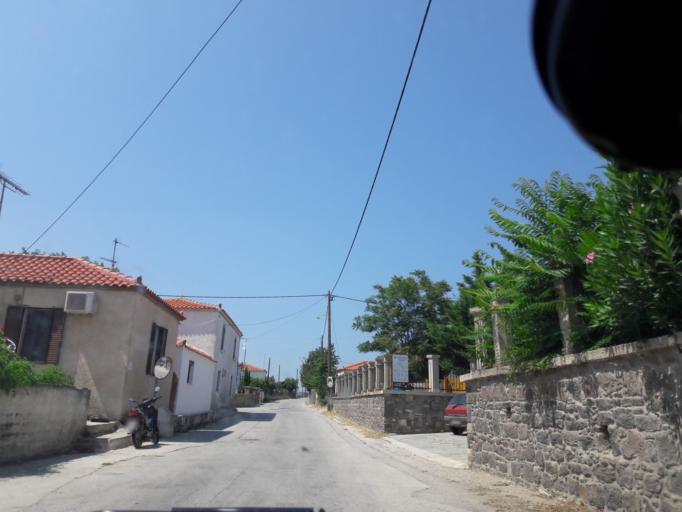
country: GR
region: North Aegean
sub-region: Nomos Lesvou
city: Myrina
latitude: 39.9239
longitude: 25.2996
